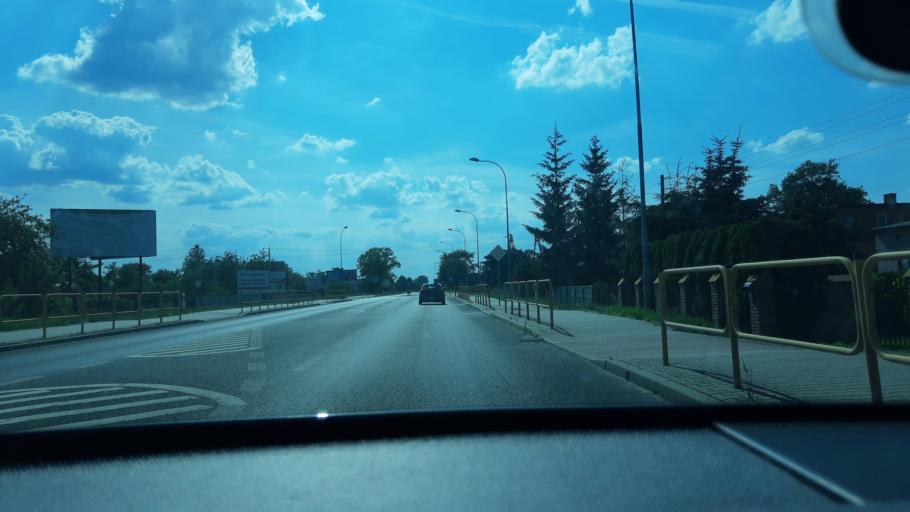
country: PL
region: Lodz Voivodeship
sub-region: Powiat zdunskowolski
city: Zdunska Wola
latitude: 51.6080
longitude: 18.8939
